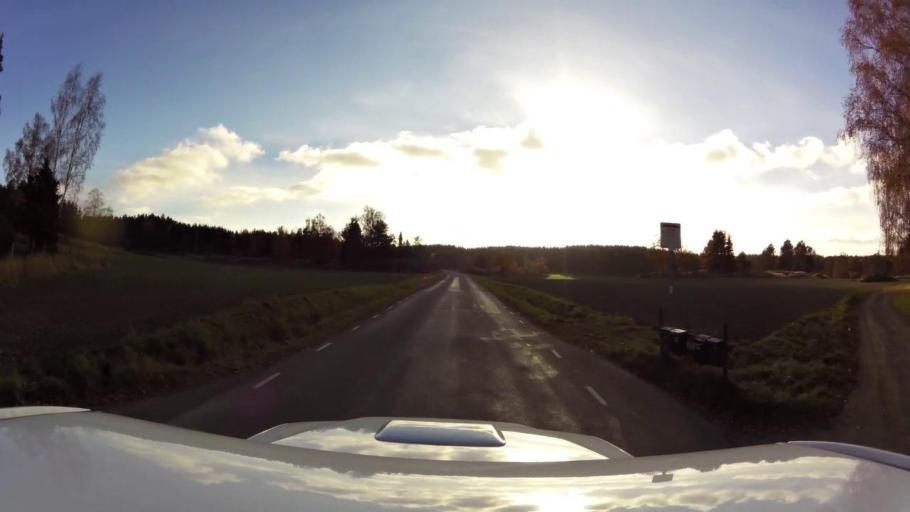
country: SE
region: OEstergoetland
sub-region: Linkopings Kommun
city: Vikingstad
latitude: 58.2816
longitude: 15.4357
